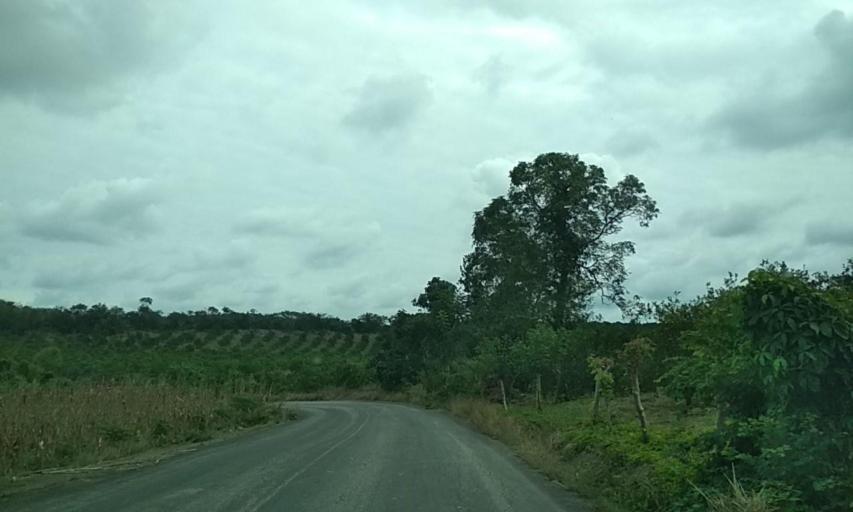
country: MX
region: Veracruz
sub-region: Papantla
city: El Chote
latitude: 20.3491
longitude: -97.3808
